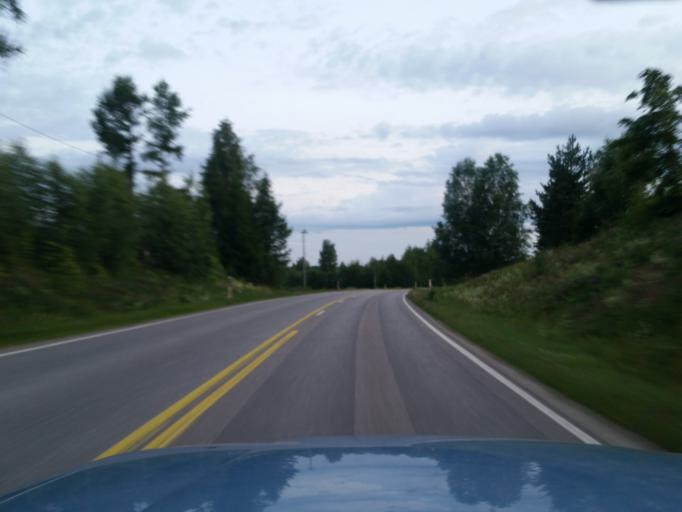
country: FI
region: Southern Savonia
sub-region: Savonlinna
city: Sulkava
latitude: 61.8177
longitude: 28.4364
